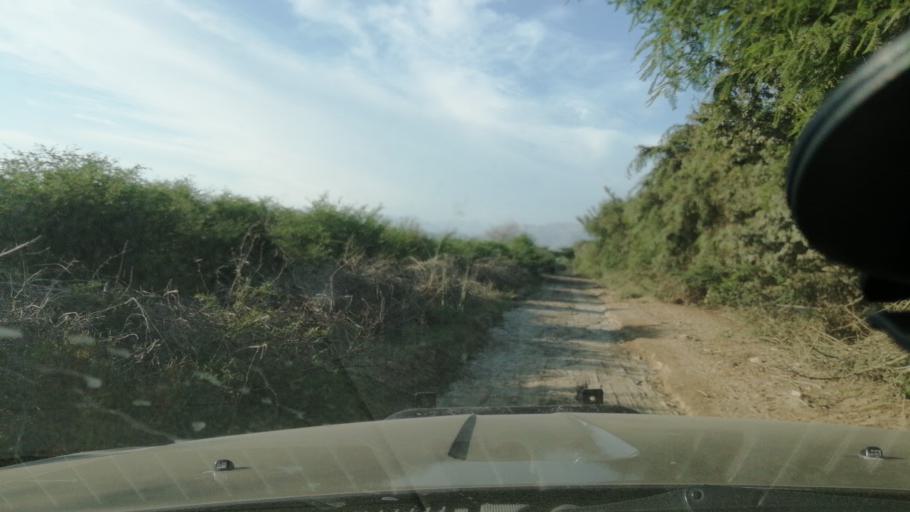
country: PE
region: Ica
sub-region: Provincia de Chincha
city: San Pedro
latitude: -13.3519
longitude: -76.1638
